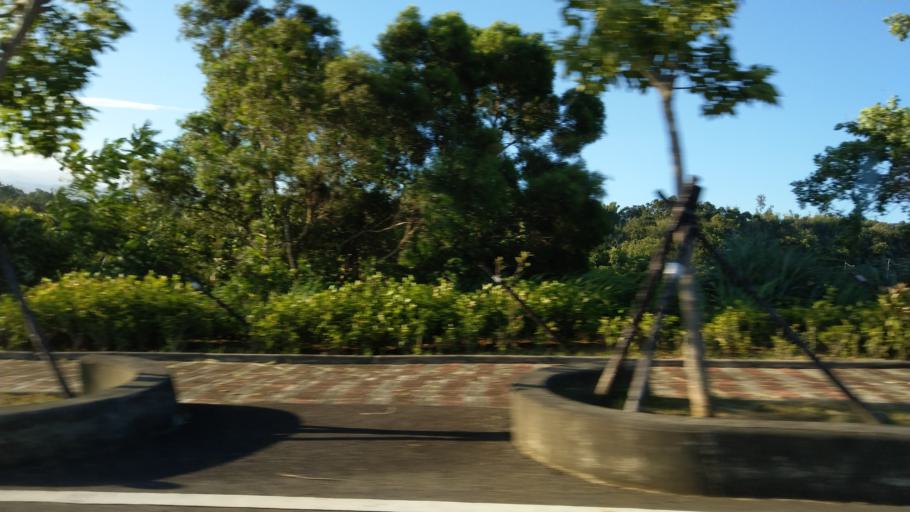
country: TW
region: Taiwan
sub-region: Miaoli
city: Miaoli
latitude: 24.5383
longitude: 120.7933
